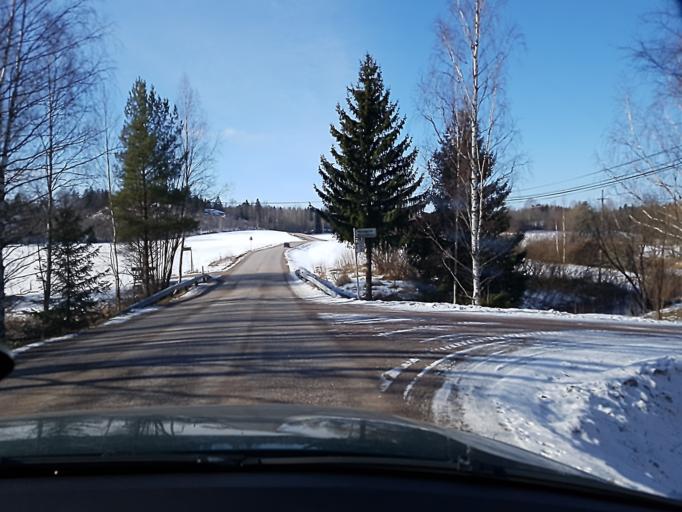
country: FI
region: Uusimaa
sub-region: Helsinki
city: Siuntio
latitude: 60.1150
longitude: 24.3117
